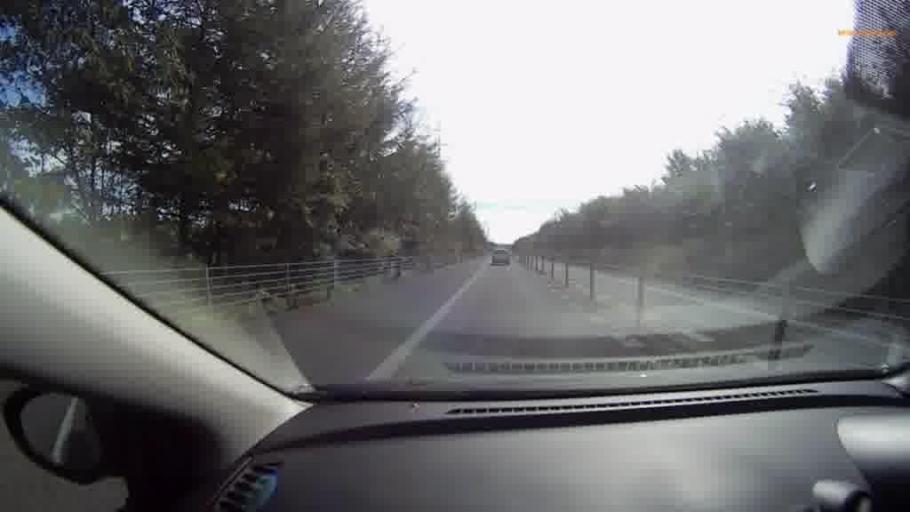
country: JP
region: Hokkaido
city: Kushiro
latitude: 43.0273
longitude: 144.4073
